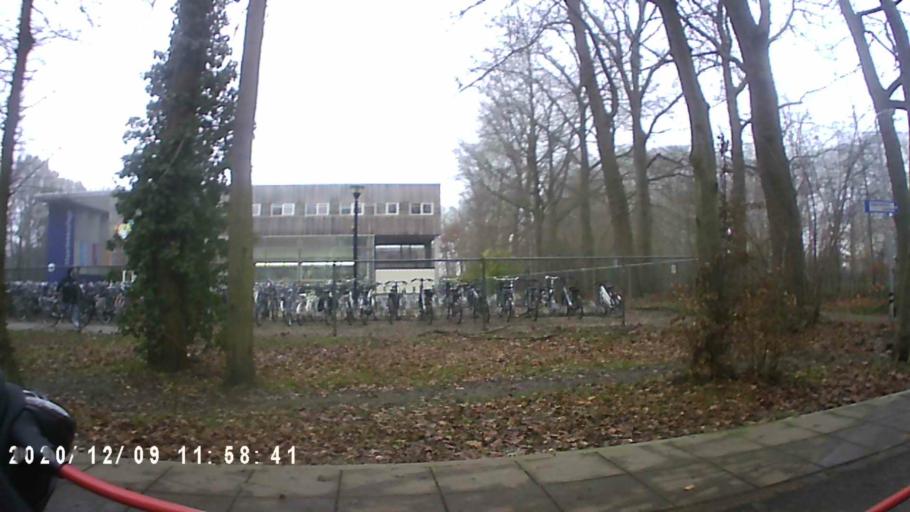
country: NL
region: Groningen
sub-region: Gemeente Haren
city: Haren
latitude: 53.1853
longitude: 6.5940
